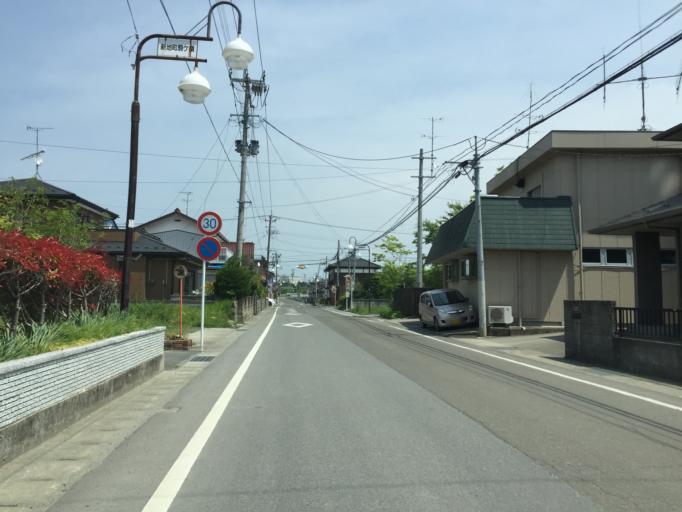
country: JP
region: Miyagi
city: Marumori
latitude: 37.8479
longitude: 140.9180
